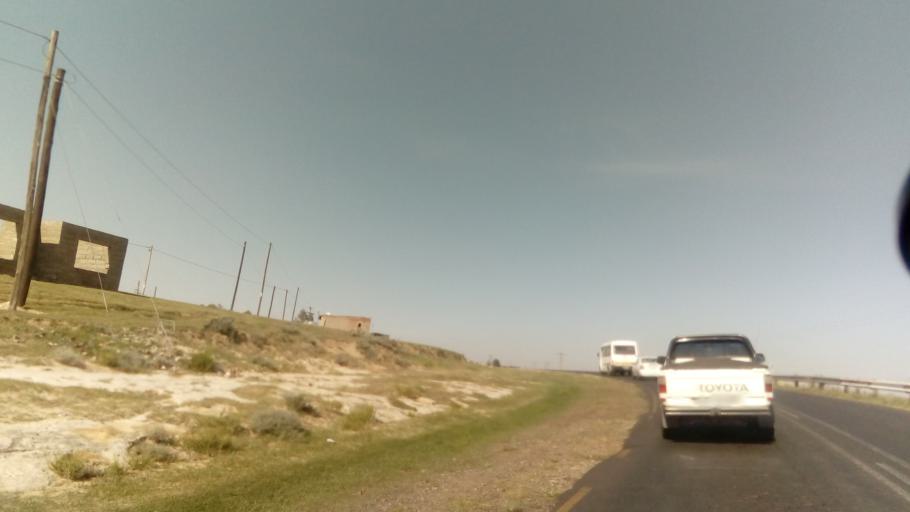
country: LS
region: Berea
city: Teyateyaneng
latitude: -29.1467
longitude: 27.6901
